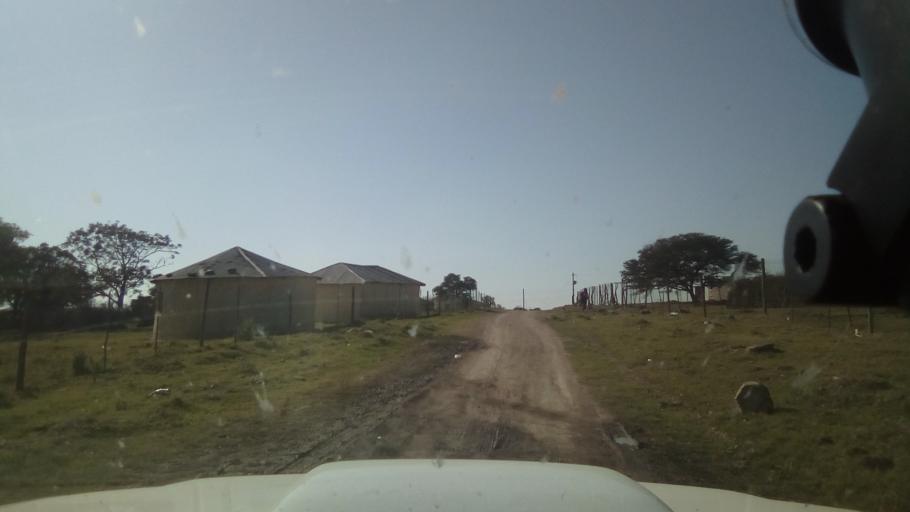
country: ZA
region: Eastern Cape
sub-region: Buffalo City Metropolitan Municipality
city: Bhisho
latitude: -32.9370
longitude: 27.3361
